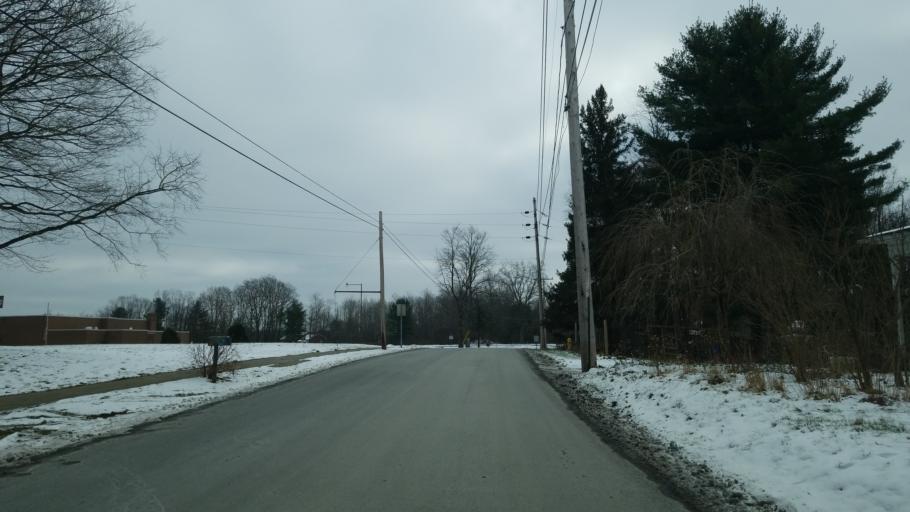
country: US
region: Pennsylvania
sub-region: Clearfield County
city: DuBois
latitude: 41.1093
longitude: -78.7612
